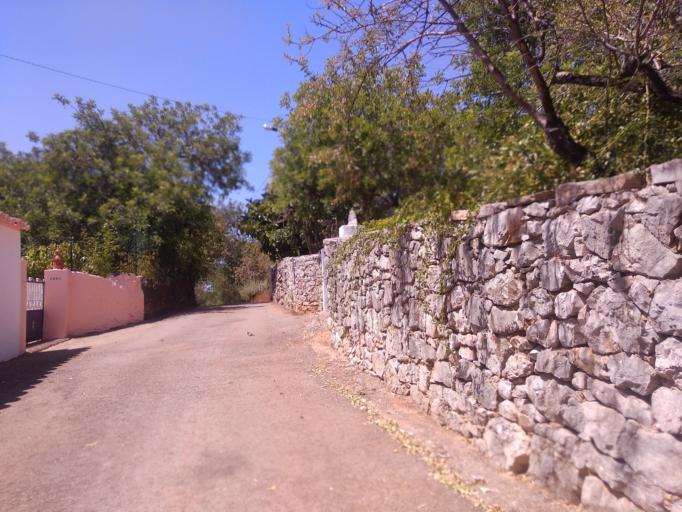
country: PT
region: Faro
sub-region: Sao Bras de Alportel
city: Sao Bras de Alportel
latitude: 37.1603
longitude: -7.9016
